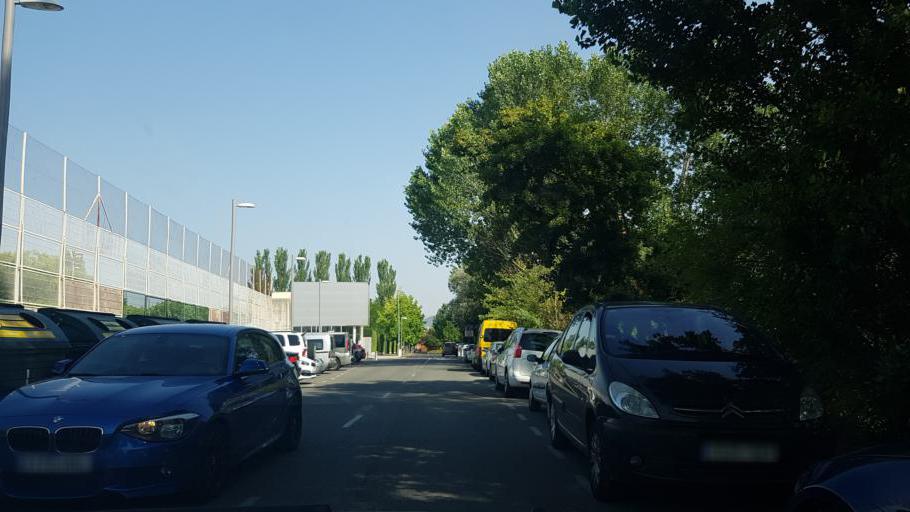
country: ES
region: Navarre
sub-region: Provincia de Navarra
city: Segundo Ensanche
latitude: 42.7903
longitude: -1.6202
